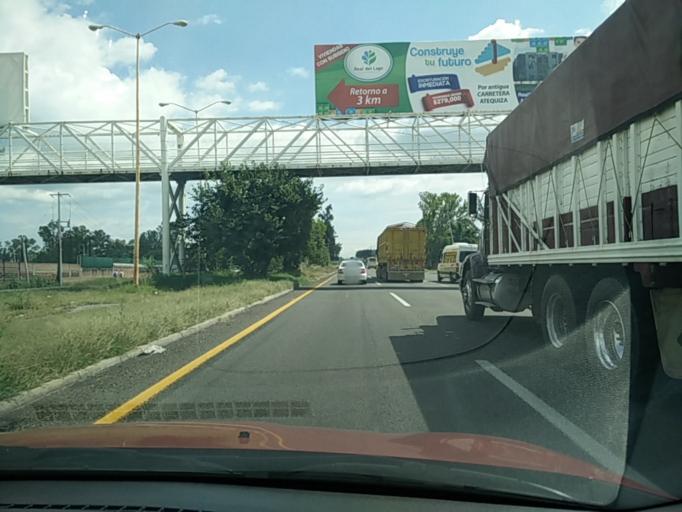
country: MX
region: Jalisco
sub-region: Ixtlahuacan de los Membrillos
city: Los Olivos
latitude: 20.4527
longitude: -103.2497
